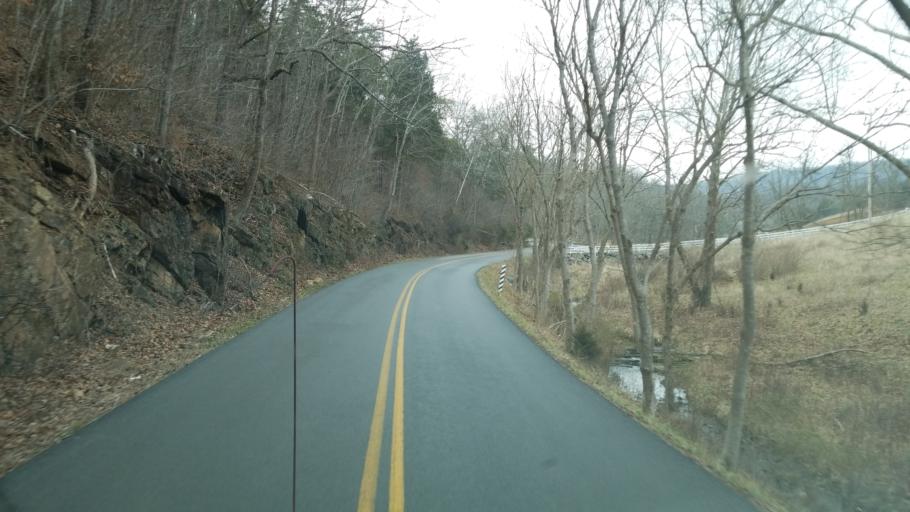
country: US
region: Virginia
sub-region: Giles County
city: Pembroke
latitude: 37.2492
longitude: -80.6857
